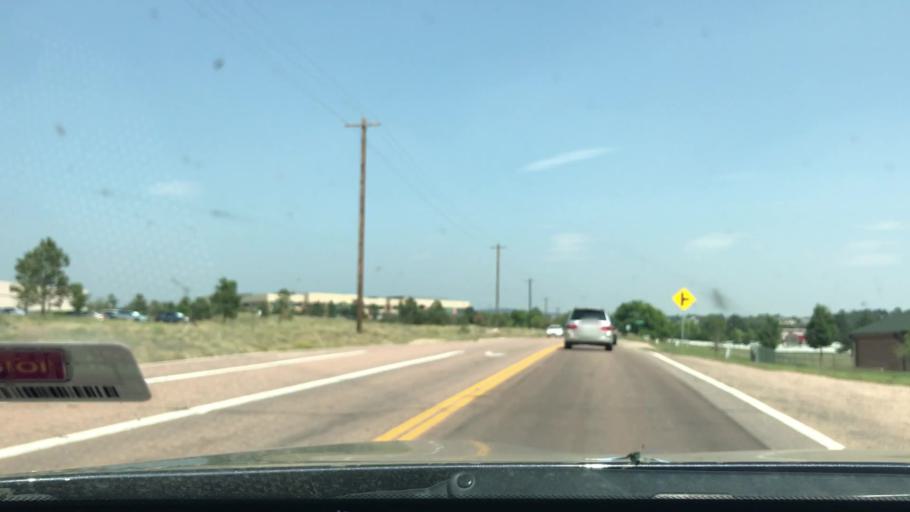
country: US
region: Colorado
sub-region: El Paso County
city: Air Force Academy
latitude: 38.9804
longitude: -104.7972
